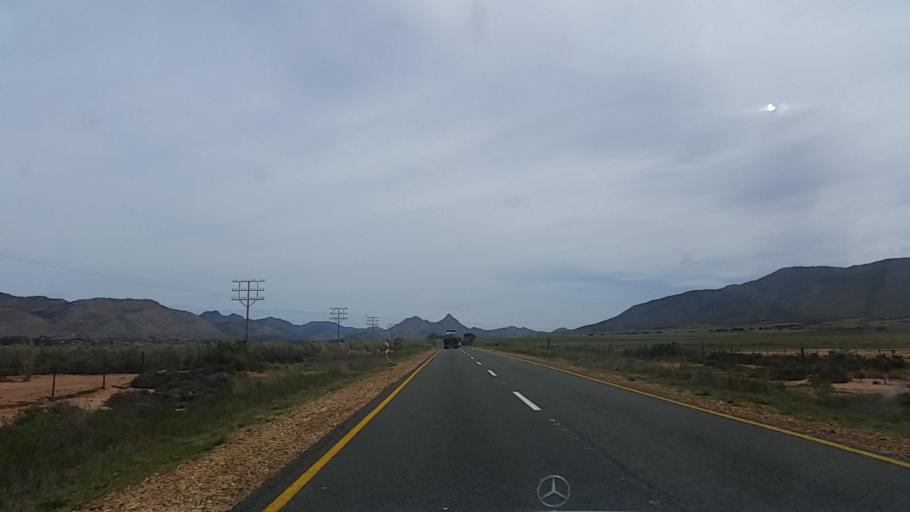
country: ZA
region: Western Cape
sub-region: Eden District Municipality
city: George
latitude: -33.8112
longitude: 22.5378
